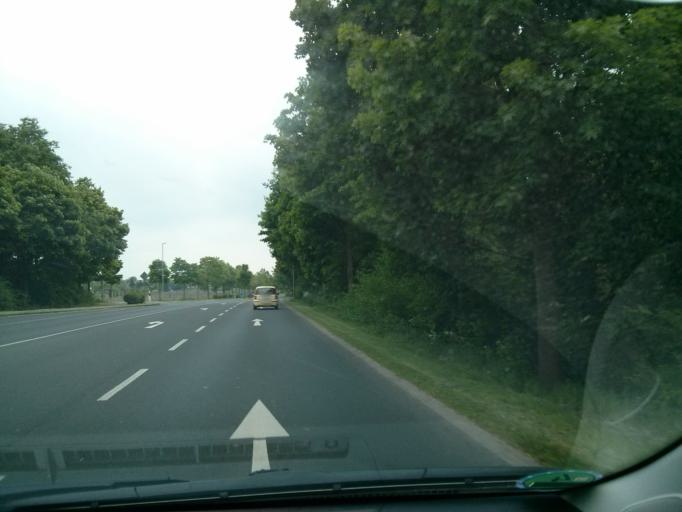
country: DE
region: North Rhine-Westphalia
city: Meckenheim
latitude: 50.6383
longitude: 7.0387
